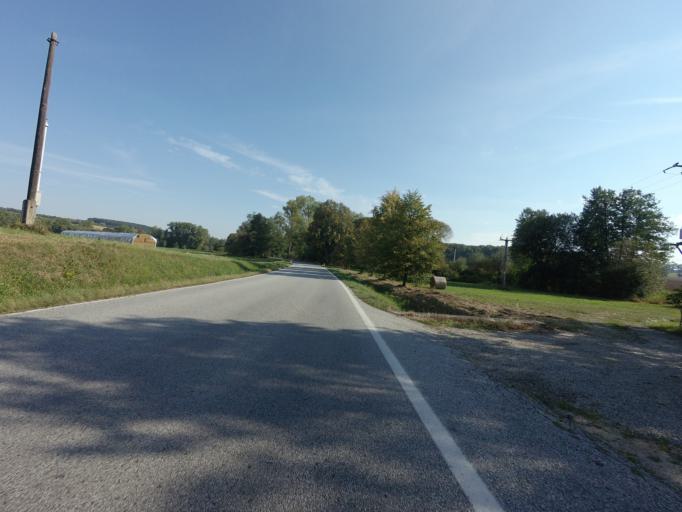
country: CZ
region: Jihocesky
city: Tyn nad Vltavou
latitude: 49.2424
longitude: 14.4203
